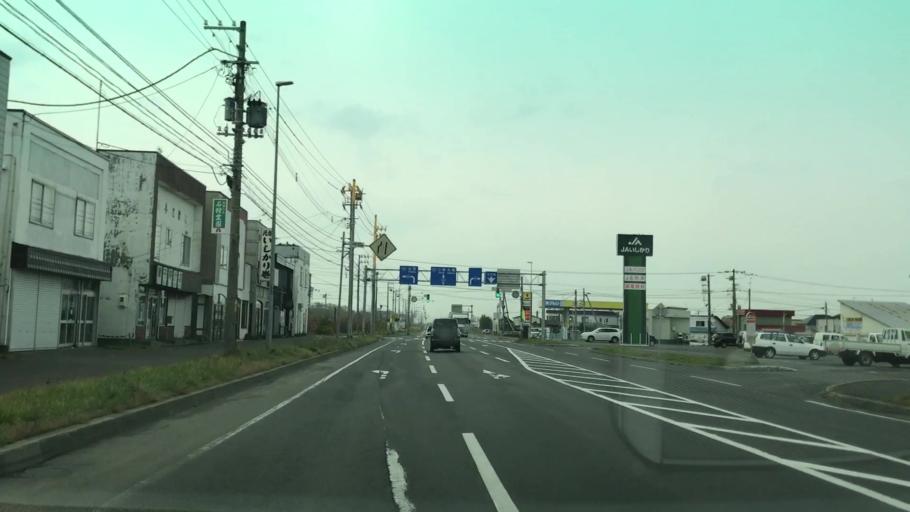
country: JP
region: Hokkaido
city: Ishikari
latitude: 43.2445
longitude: 141.3715
